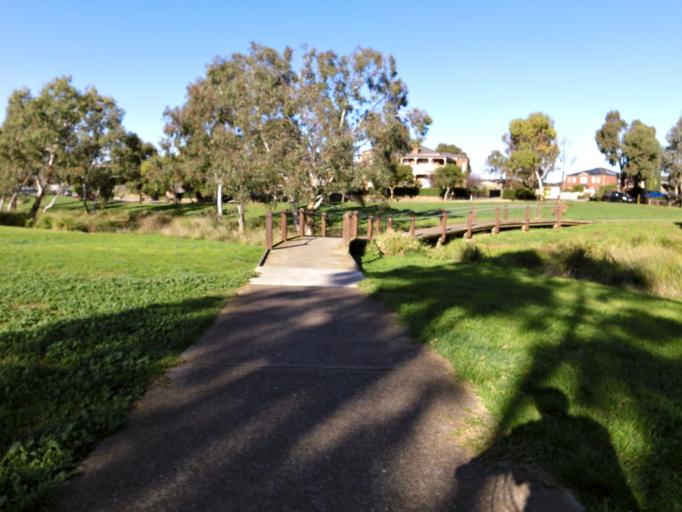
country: AU
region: Victoria
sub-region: Wyndham
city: Hoppers Crossing
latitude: -37.8449
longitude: 144.7051
